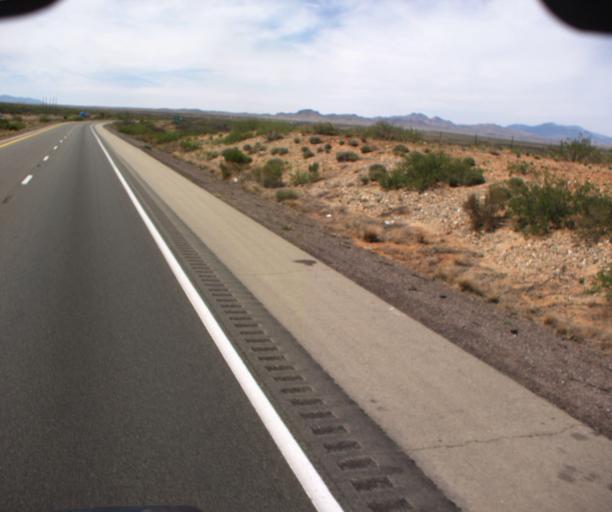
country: US
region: Arizona
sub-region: Cochise County
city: Willcox
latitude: 32.3470
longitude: -109.5975
